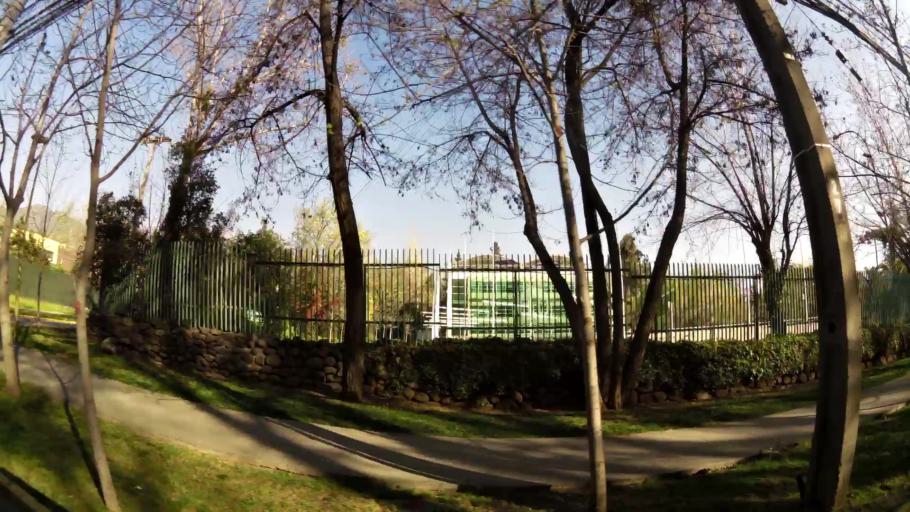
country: CL
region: Santiago Metropolitan
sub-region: Provincia de Santiago
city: Villa Presidente Frei, Nunoa, Santiago, Chile
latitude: -33.3746
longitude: -70.5043
